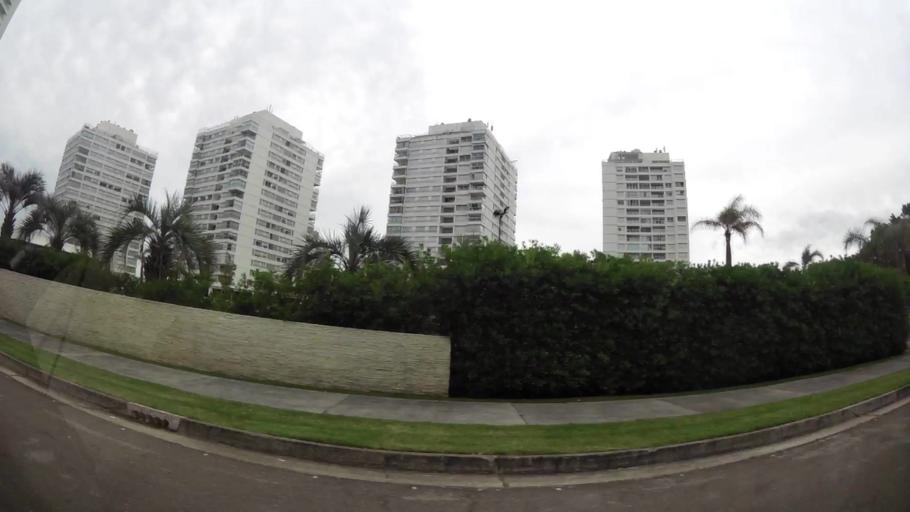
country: UY
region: Maldonado
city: Maldonado
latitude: -34.9269
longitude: -54.9595
